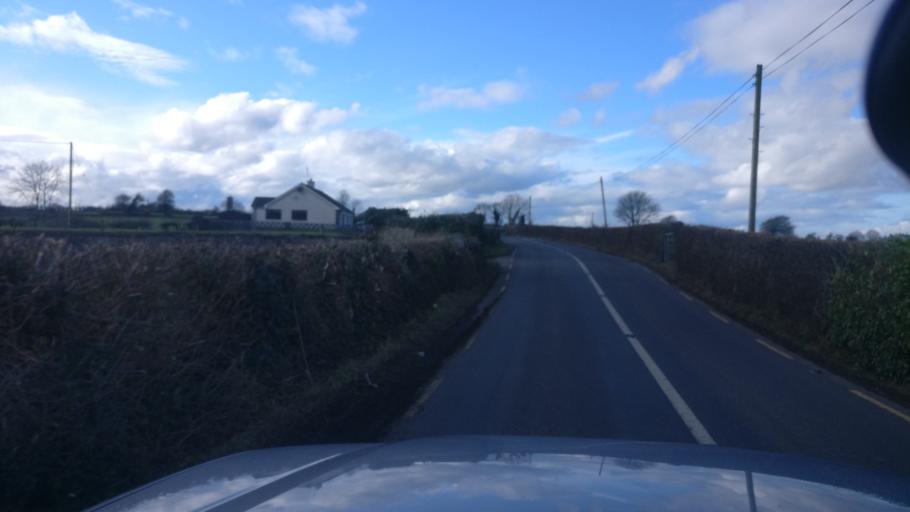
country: IE
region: Connaught
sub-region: County Galway
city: Loughrea
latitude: 53.1654
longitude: -8.3874
